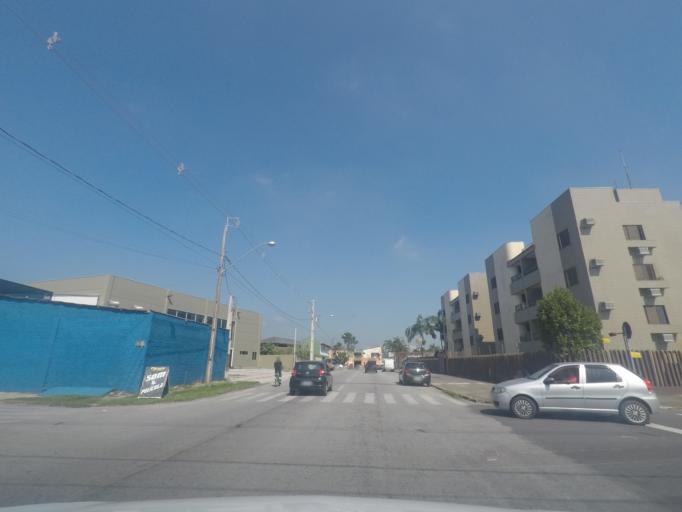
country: BR
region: Parana
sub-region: Paranagua
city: Paranagua
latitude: -25.5300
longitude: -48.5216
